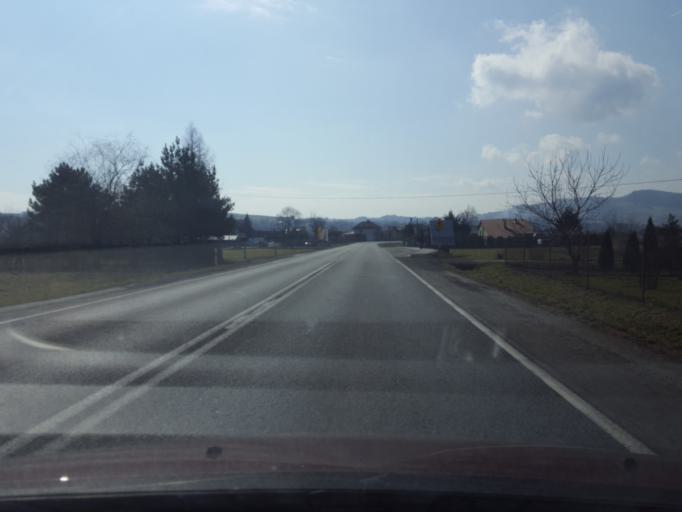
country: PL
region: Lesser Poland Voivodeship
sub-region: Powiat nowosadecki
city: Lososina Dolna
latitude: 49.7586
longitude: 20.6352
